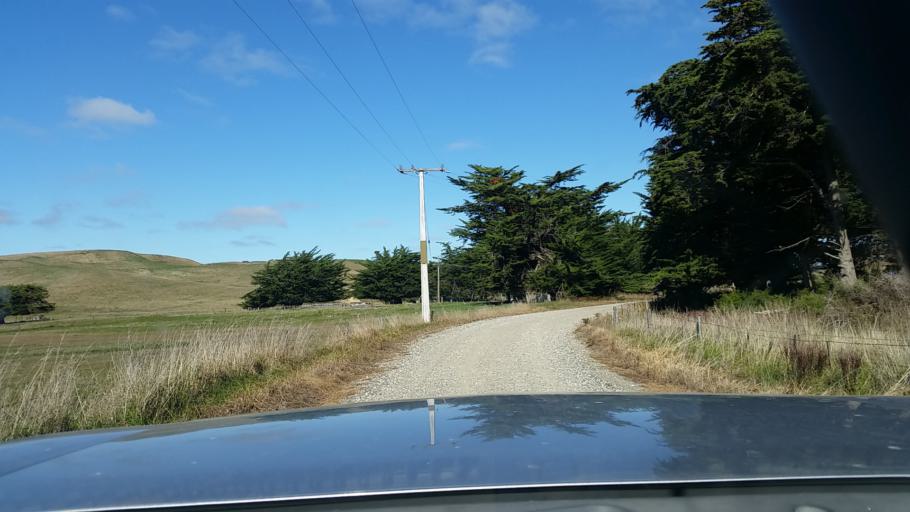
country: NZ
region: Marlborough
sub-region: Marlborough District
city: Blenheim
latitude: -41.7426
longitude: 174.1564
